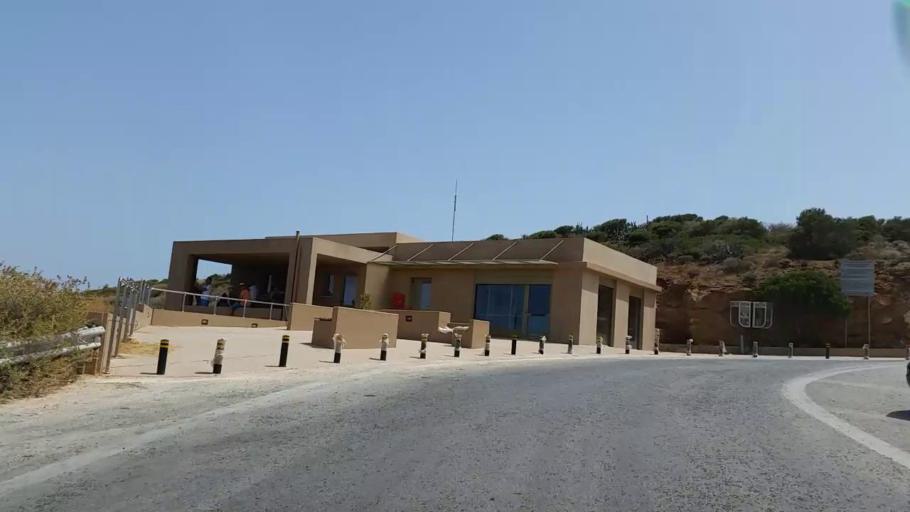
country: GR
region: Attica
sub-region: Nomarchia Anatolikis Attikis
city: Lavrio
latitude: 37.6506
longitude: 24.0273
